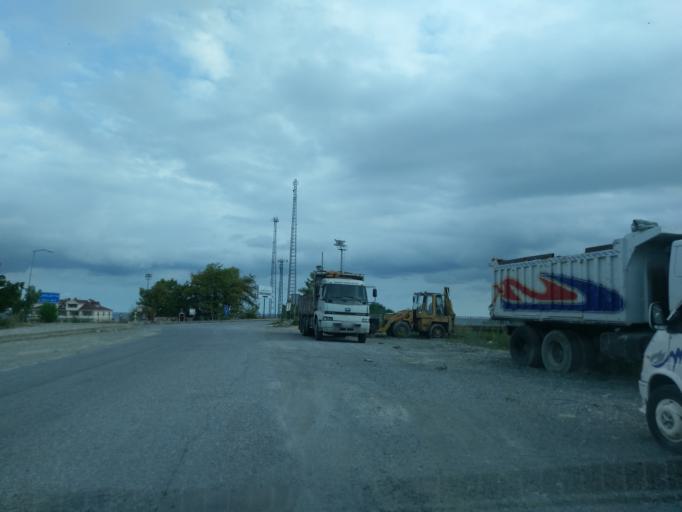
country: TR
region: Kastamonu
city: Catalzeytin
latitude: 41.9522
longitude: 34.2268
